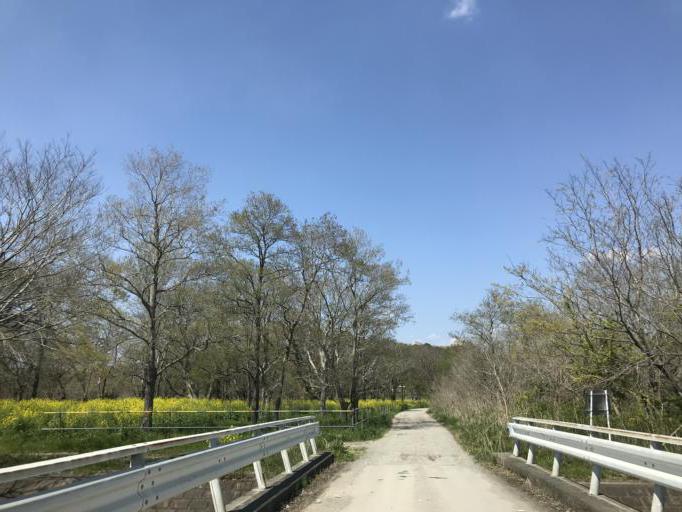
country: JP
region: Ibaraki
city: Moriya
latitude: 35.9201
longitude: 139.9917
